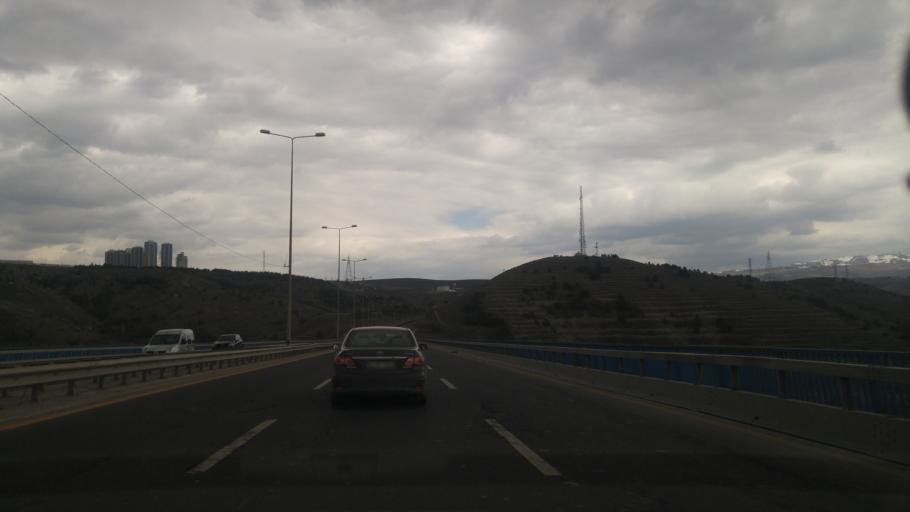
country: TR
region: Ankara
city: Mamak
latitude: 39.8892
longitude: 32.9071
